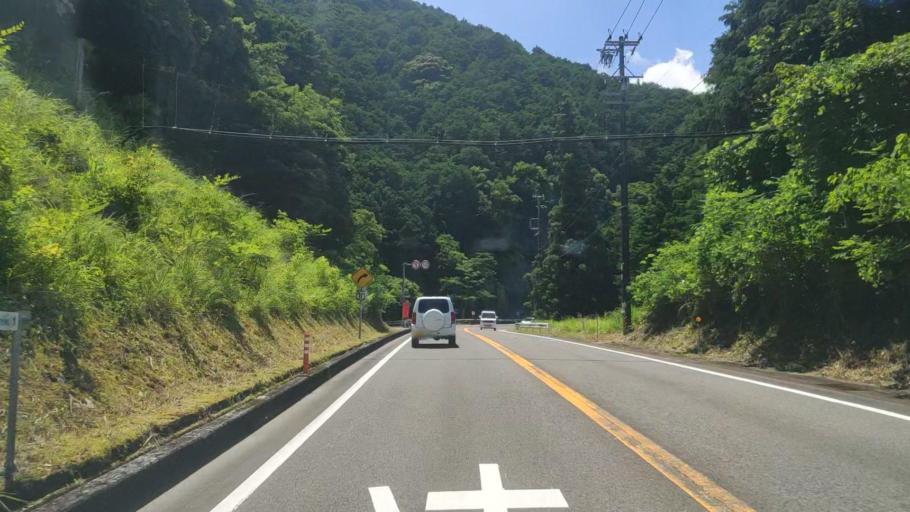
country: JP
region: Mie
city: Owase
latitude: 34.1024
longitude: 136.2055
